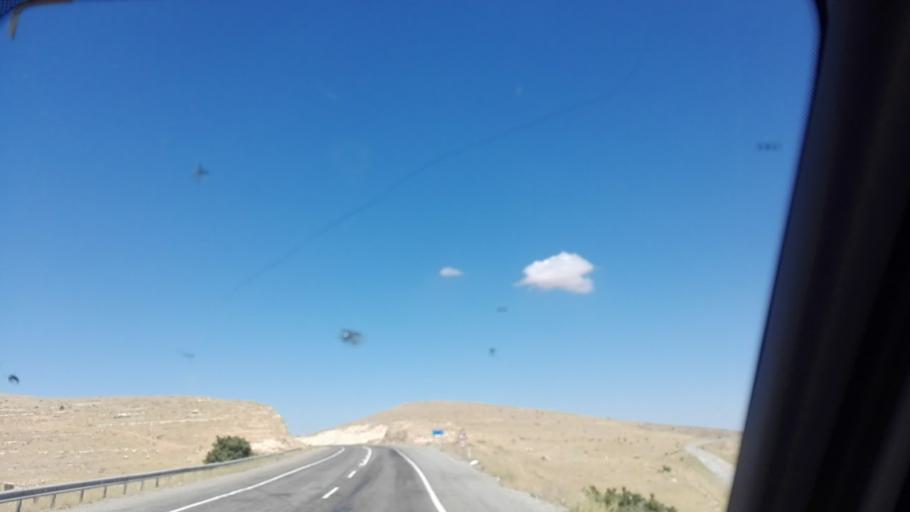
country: TR
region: Batman
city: Gerdzhyush
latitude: 37.5549
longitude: 41.3632
